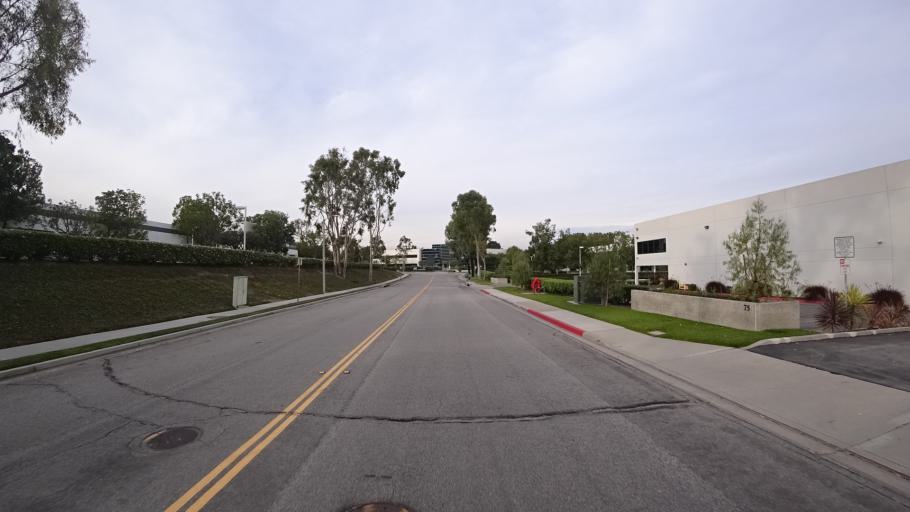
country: US
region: California
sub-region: Orange County
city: Laguna Woods
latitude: 33.5930
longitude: -117.7241
